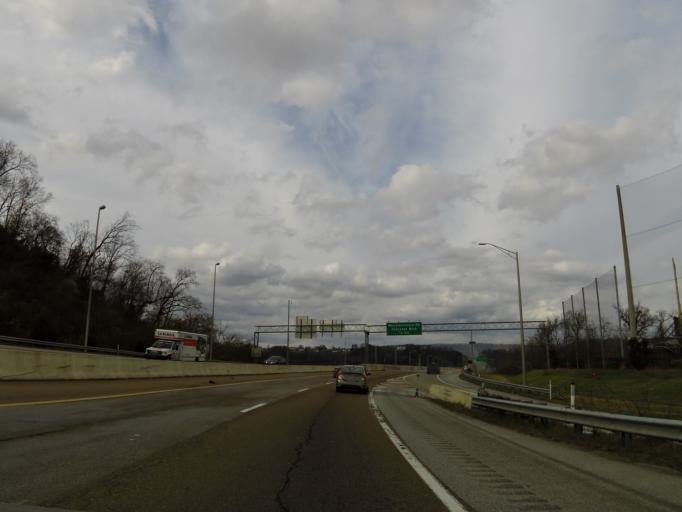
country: US
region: Tennessee
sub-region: Hamilton County
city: Chattanooga
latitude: 35.0536
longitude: -85.3149
